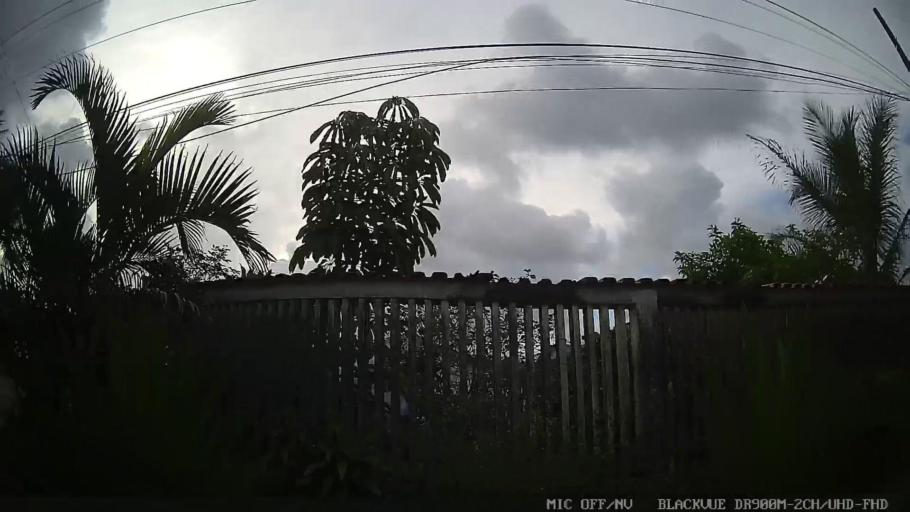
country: BR
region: Sao Paulo
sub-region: Itanhaem
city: Itanhaem
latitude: -24.1567
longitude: -46.7407
